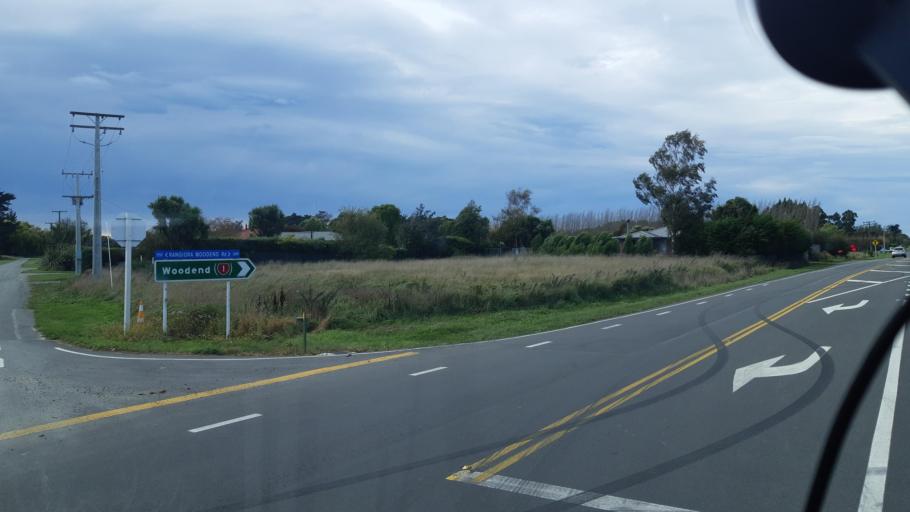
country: NZ
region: Canterbury
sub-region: Waimakariri District
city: Woodend
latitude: -43.3078
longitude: 172.6348
